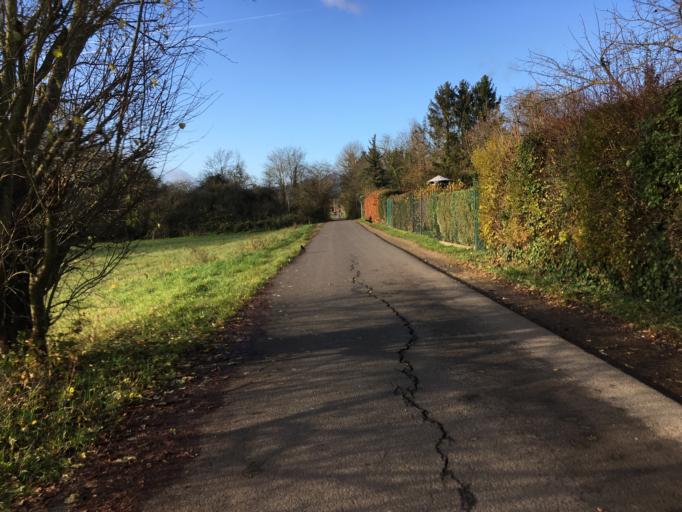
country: DE
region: Hesse
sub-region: Regierungsbezirk Darmstadt
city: Wiesbaden
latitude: 50.0567
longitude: 8.2323
